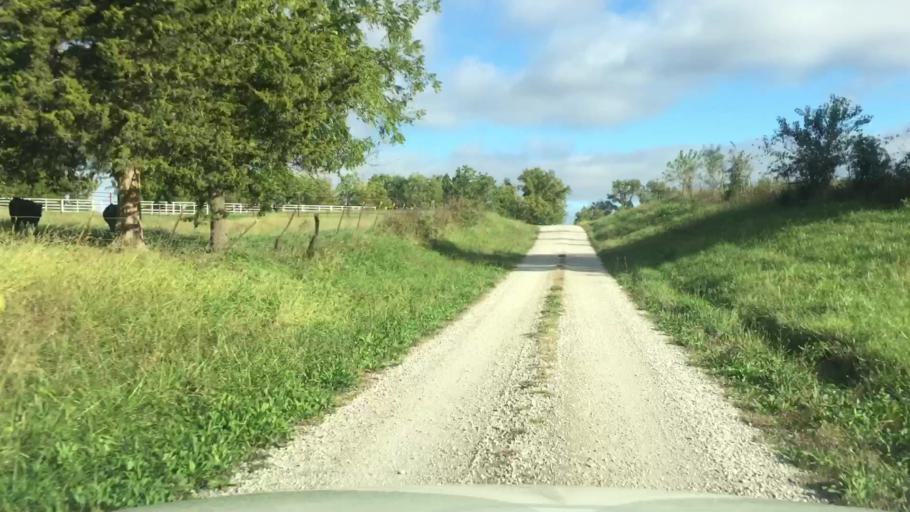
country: US
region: Missouri
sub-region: Howard County
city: New Franklin
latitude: 39.1024
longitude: -92.7793
